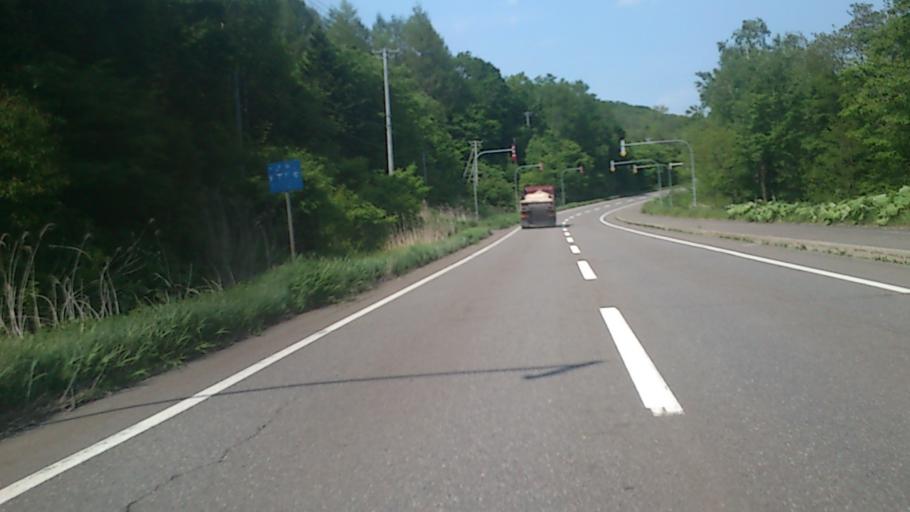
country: JP
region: Hokkaido
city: Otofuke
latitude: 43.2526
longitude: 143.5657
